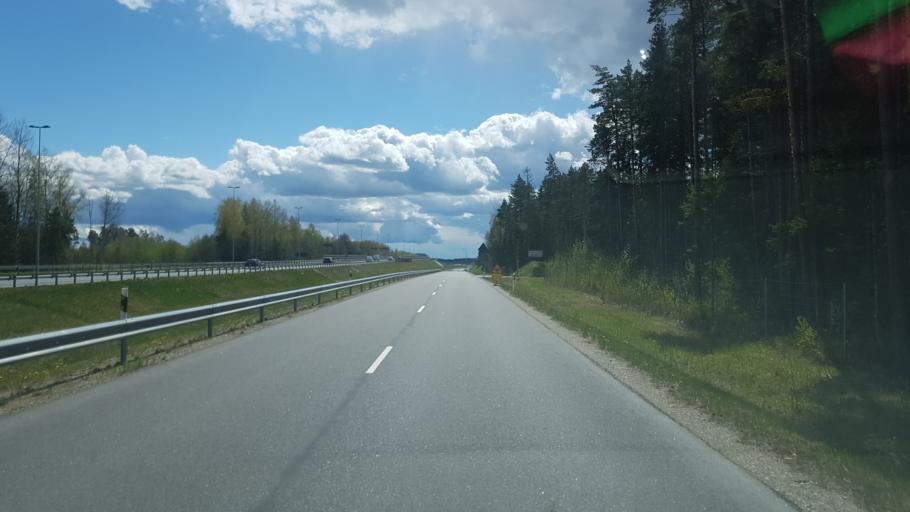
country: EE
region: Harju
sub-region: Rae vald
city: Vaida
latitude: 59.2254
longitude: 25.0326
